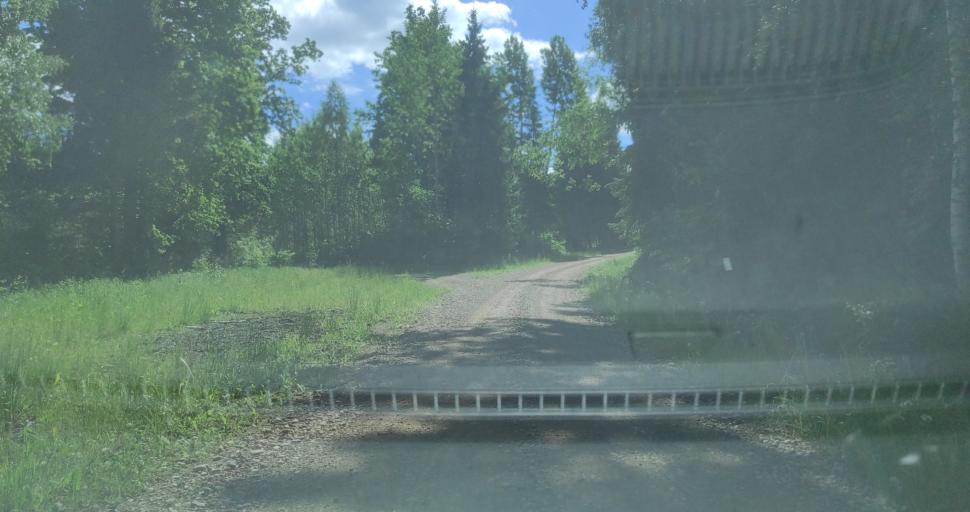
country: LV
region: Alsunga
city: Alsunga
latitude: 56.8843
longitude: 21.7257
